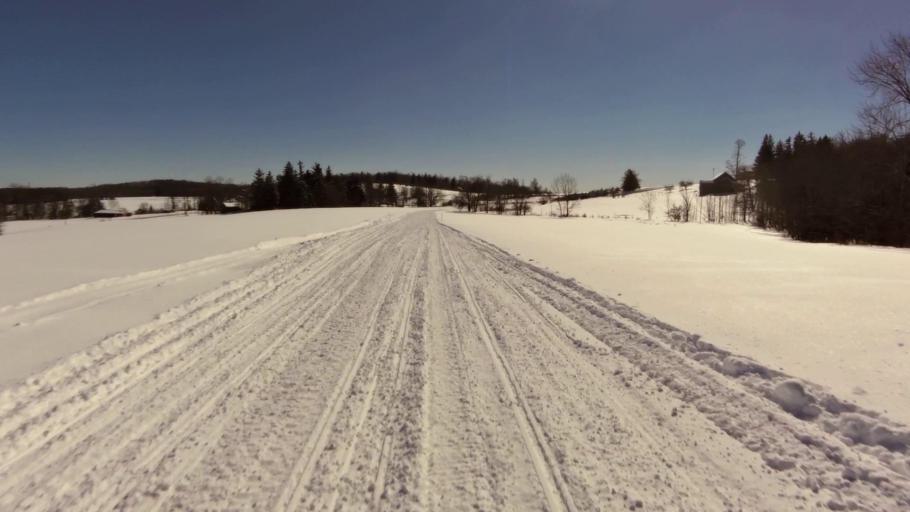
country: US
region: New York
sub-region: Chautauqua County
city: Mayville
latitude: 42.2211
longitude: -79.5191
